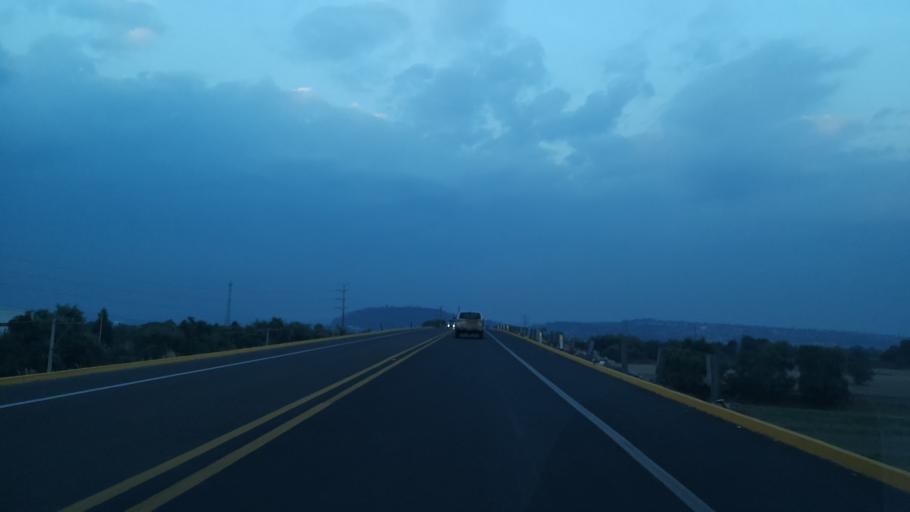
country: MX
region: Puebla
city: Santa Ana Xalmimilulco
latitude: 19.2065
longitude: -98.3613
